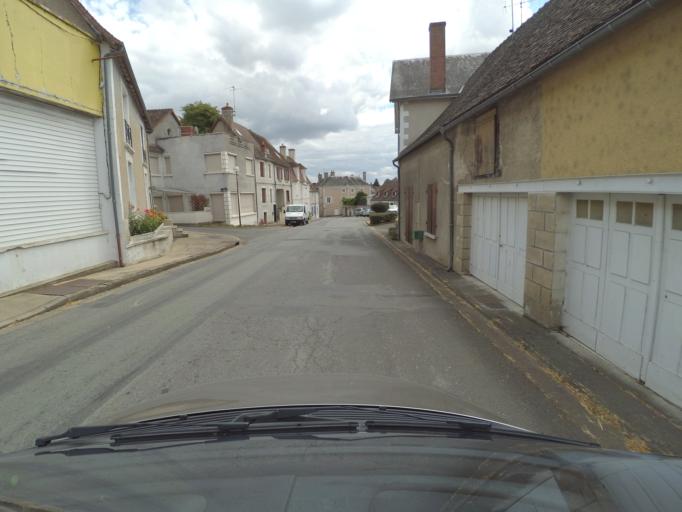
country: FR
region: Centre
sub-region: Departement de l'Indre
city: Belabre
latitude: 46.4677
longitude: 1.0411
